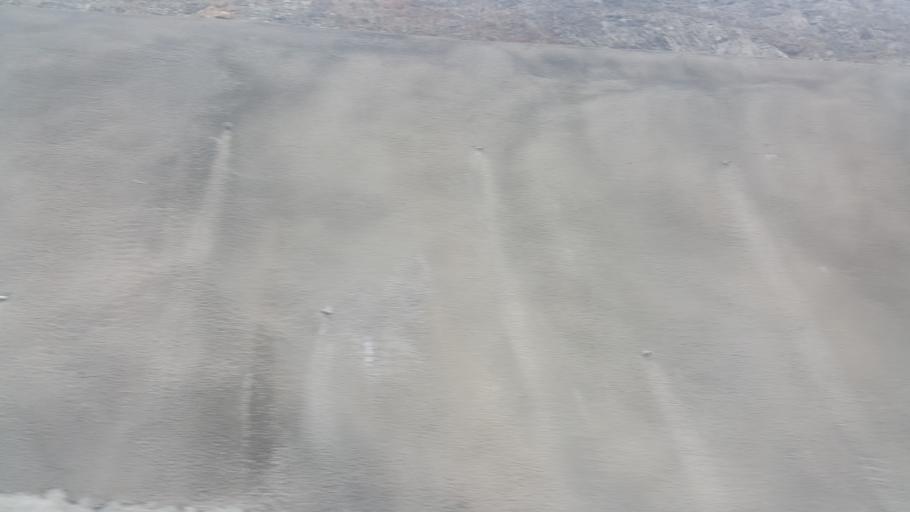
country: TR
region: Nigde
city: Ciftehan
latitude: 37.5359
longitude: 34.7994
